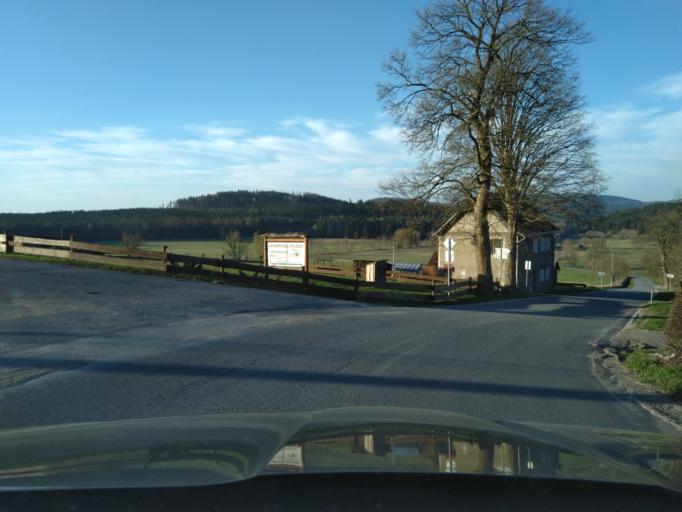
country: CZ
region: Jihocesky
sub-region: Okres Prachatice
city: Volary
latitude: 48.9438
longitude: 13.7998
